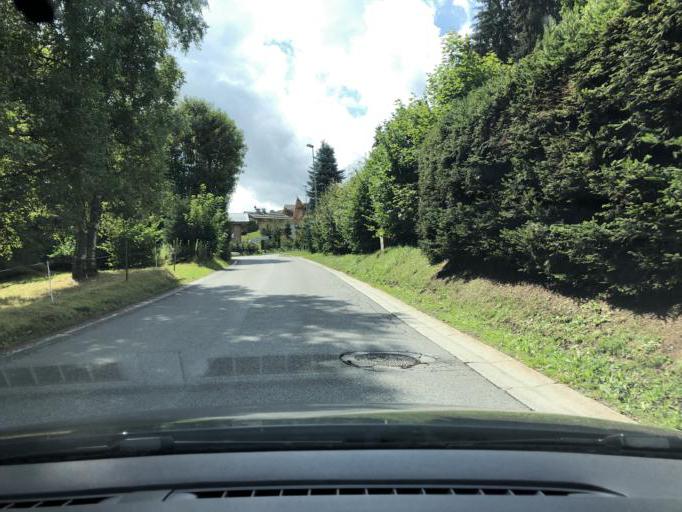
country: FR
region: Rhone-Alpes
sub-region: Departement de la Haute-Savoie
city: Combloux
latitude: 45.8921
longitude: 6.6349
